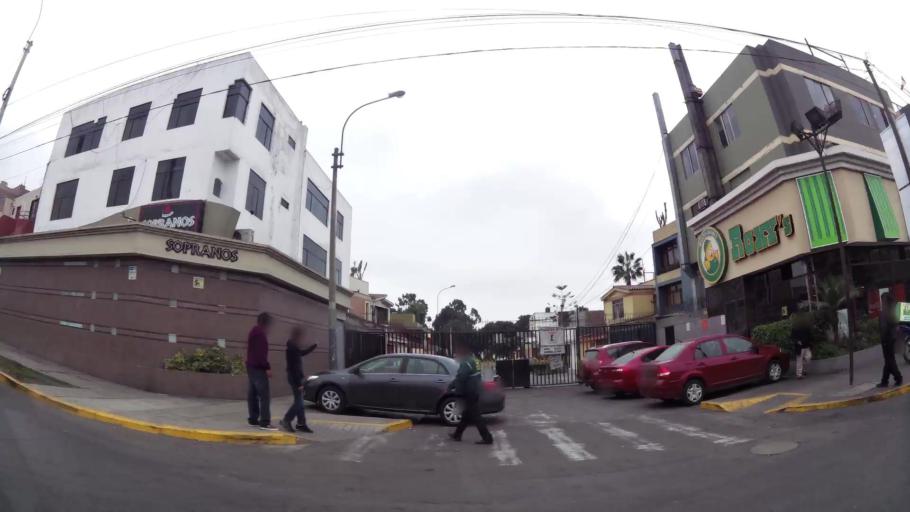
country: PE
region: Lima
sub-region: Lima
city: San Luis
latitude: -12.0817
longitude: -76.9957
